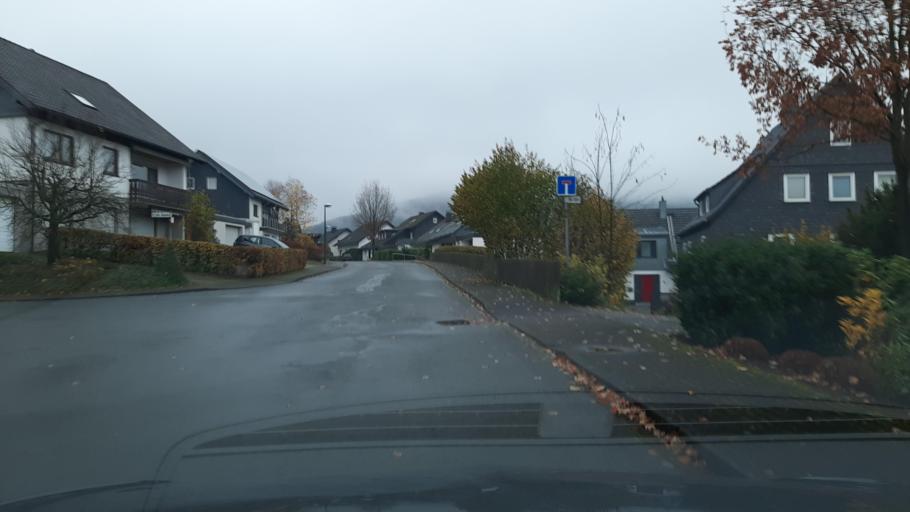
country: DE
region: North Rhine-Westphalia
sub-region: Regierungsbezirk Arnsberg
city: Olsberg
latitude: 51.2920
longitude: 8.5048
